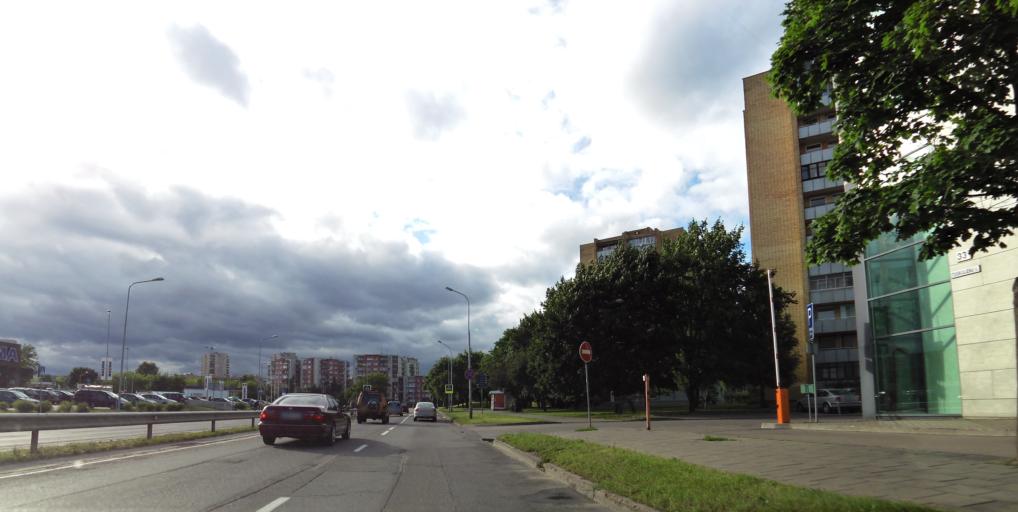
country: LT
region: Vilnius County
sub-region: Vilnius
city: Vilnius
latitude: 54.7021
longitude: 25.2906
